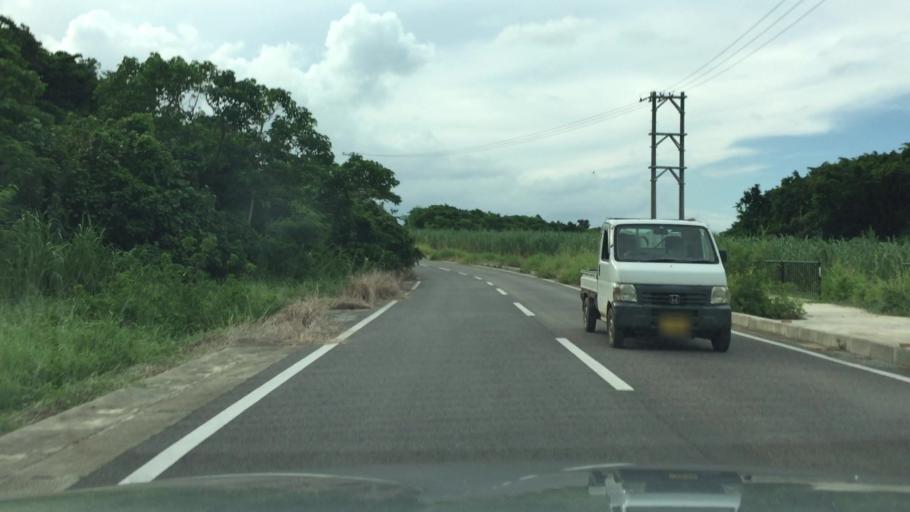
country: JP
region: Okinawa
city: Ishigaki
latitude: 24.4675
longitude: 124.1403
